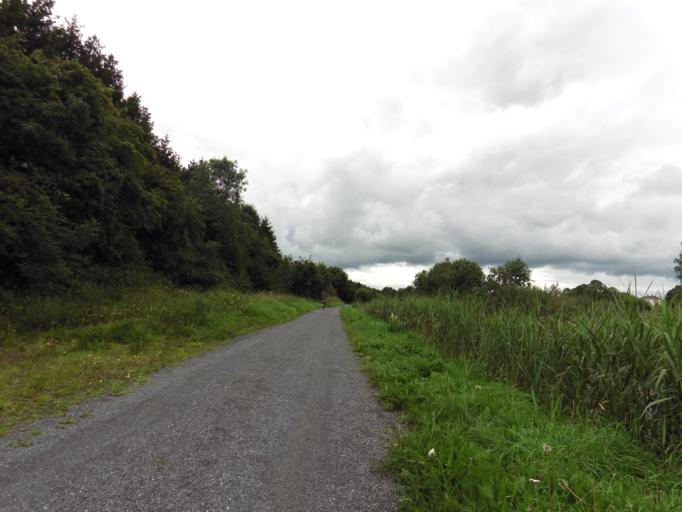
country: IE
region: Leinster
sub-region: An Iarmhi
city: An Muileann gCearr
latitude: 53.5199
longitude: -7.4395
